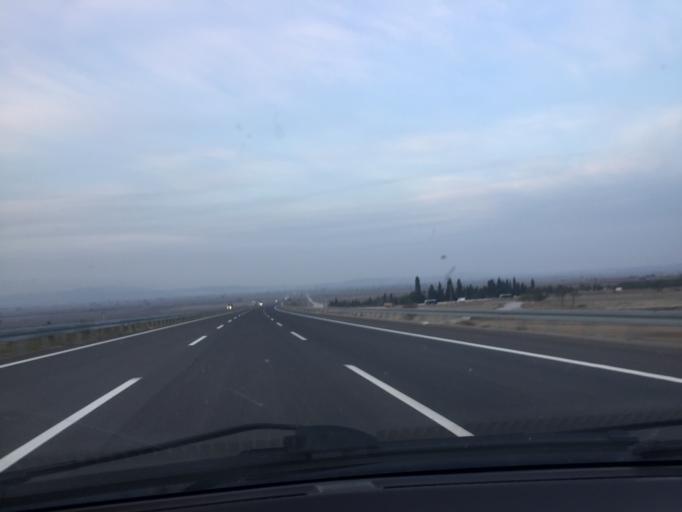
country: TR
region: Manisa
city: Halitpasa
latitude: 38.7011
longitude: 27.6435
